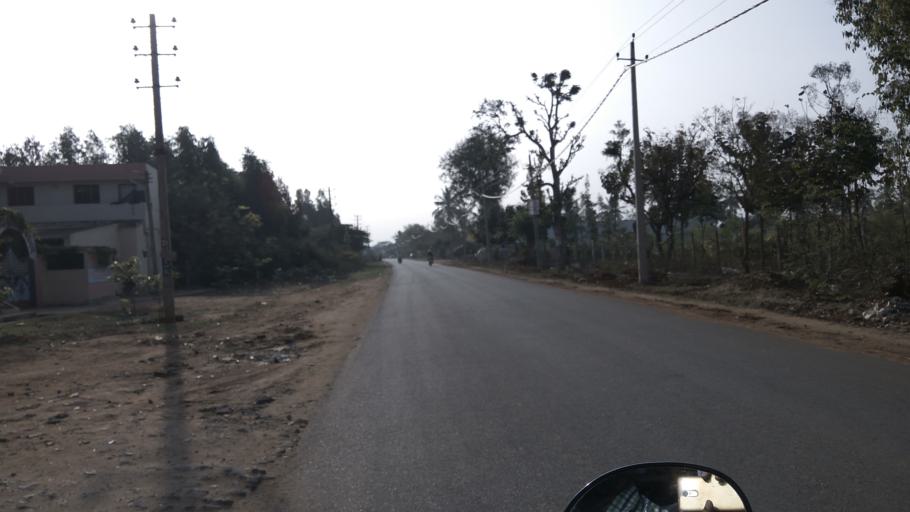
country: IN
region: Karnataka
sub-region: Kolar
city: Kolar
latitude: 13.1205
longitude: 78.1691
